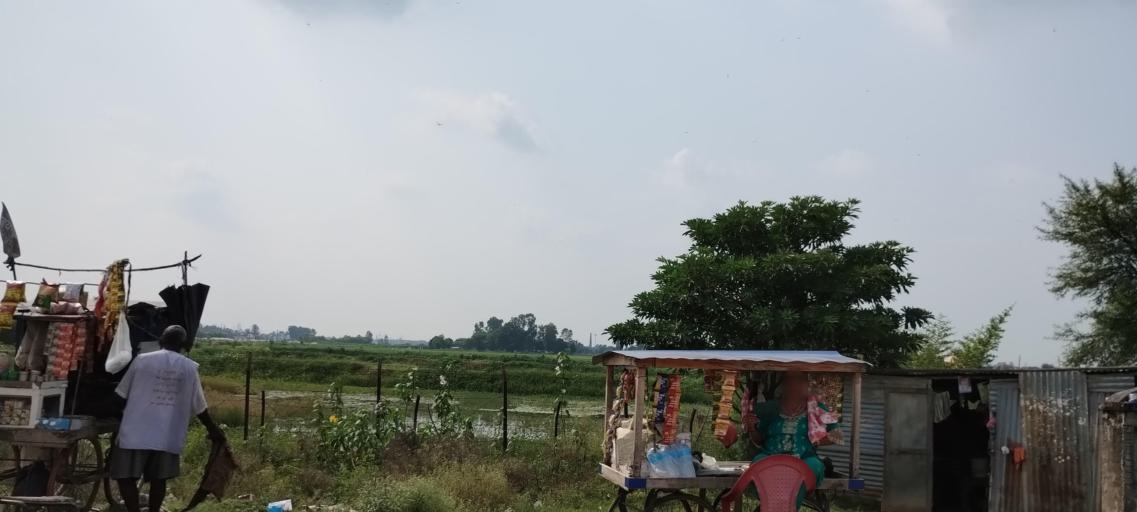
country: NP
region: Mid Western
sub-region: Bheri Zone
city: Nepalgunj
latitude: 28.1017
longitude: 81.6541
